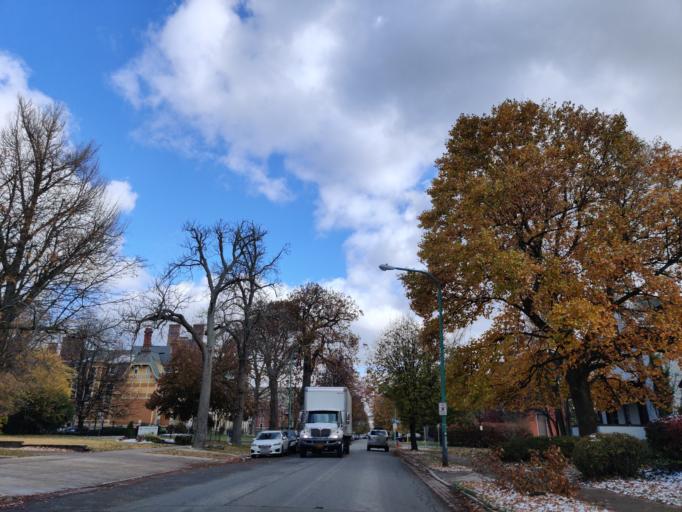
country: US
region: New York
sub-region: Erie County
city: Buffalo
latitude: 42.9023
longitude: -78.8798
